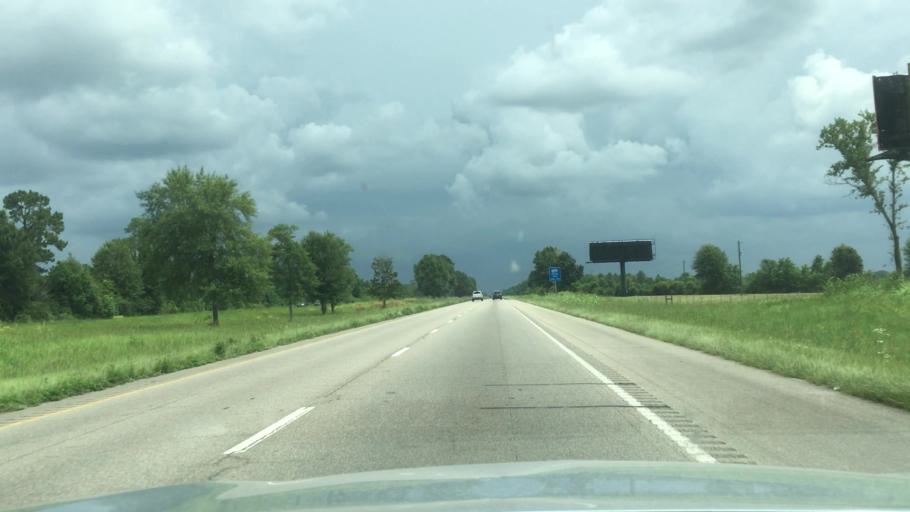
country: US
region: Mississippi
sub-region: Pearl River County
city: Carriere
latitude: 30.5787
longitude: -89.6301
